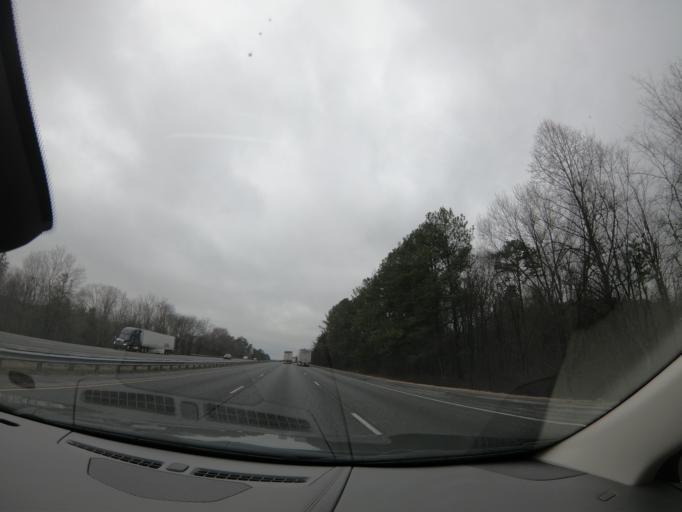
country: US
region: Georgia
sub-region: Gordon County
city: Calhoun
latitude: 34.5934
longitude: -84.9546
